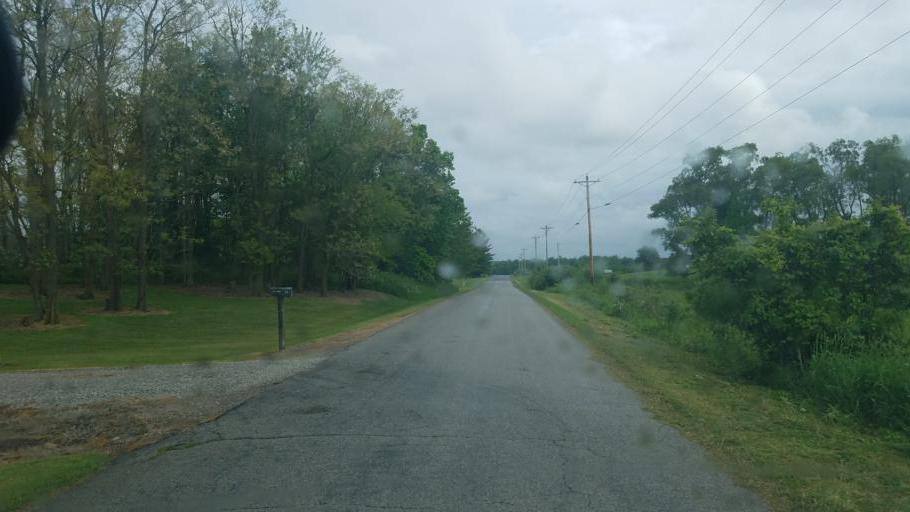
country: US
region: Ohio
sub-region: Knox County
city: Fredericktown
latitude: 40.4740
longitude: -82.6467
